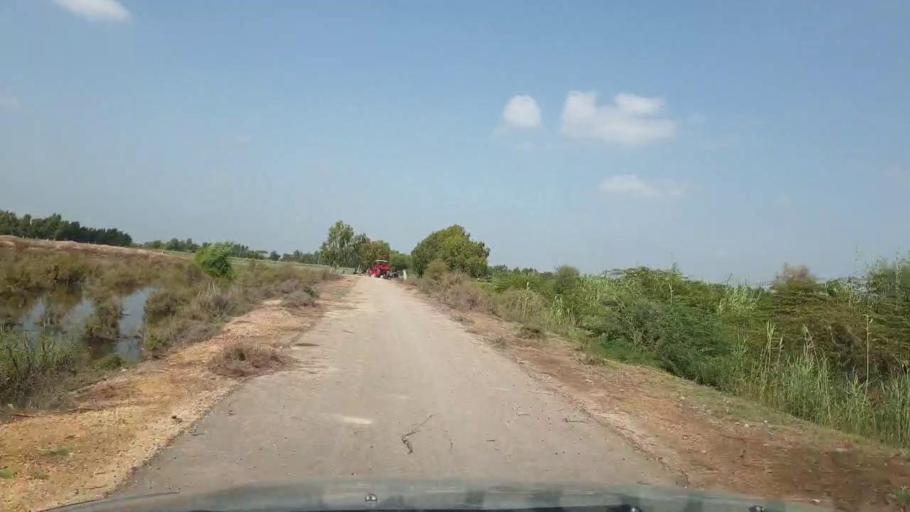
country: PK
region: Sindh
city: Rajo Khanani
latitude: 25.0342
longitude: 68.9364
